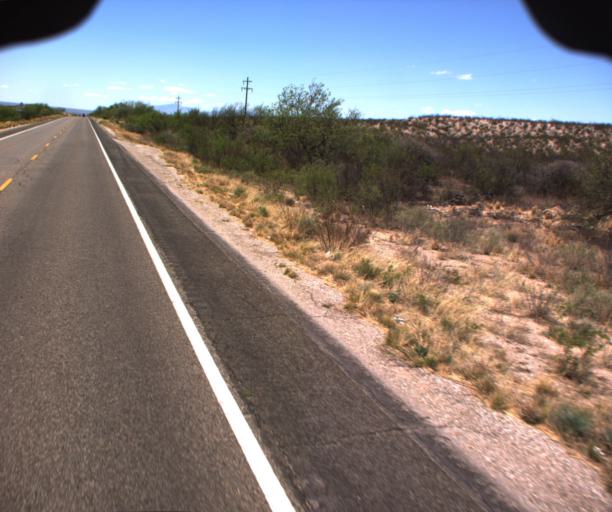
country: US
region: Arizona
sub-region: Cochise County
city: Tombstone
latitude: 31.7781
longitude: -110.1345
